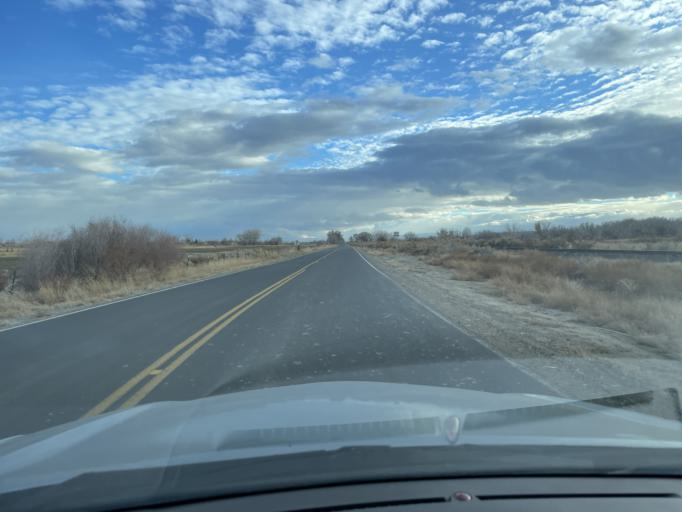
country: US
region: Colorado
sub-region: Montrose County
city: Olathe
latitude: 38.6423
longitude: -107.9930
